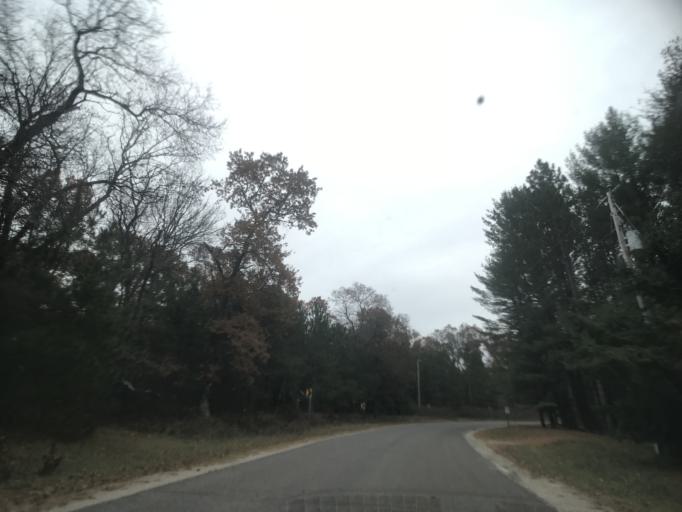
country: US
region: Wisconsin
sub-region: Oconto County
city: Gillett
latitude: 45.2693
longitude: -88.2545
